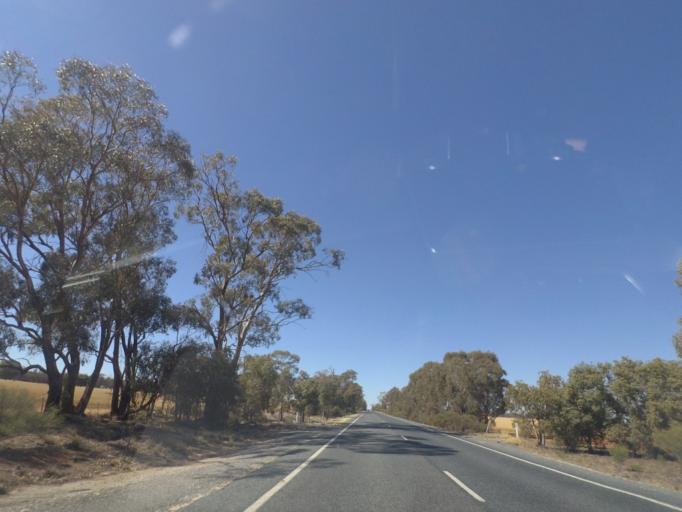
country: AU
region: New South Wales
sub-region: Bland
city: West Wyalong
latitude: -34.1586
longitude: 147.1172
